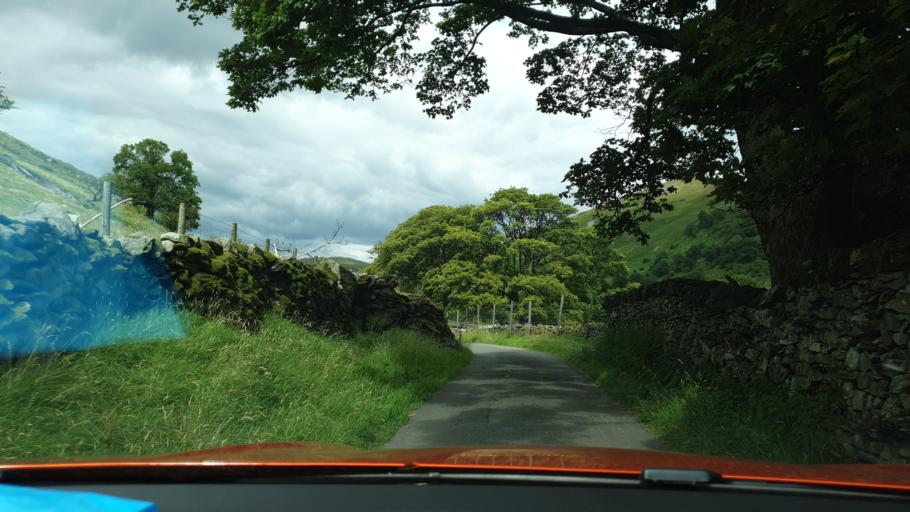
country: GB
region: England
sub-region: Cumbria
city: Ambleside
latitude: 54.5448
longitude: -2.8738
